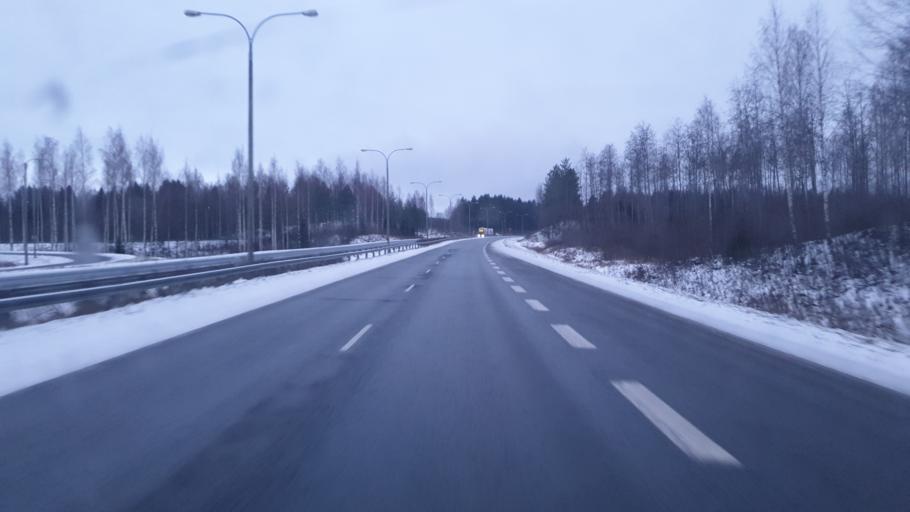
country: FI
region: Northern Savo
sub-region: Kuopio
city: Siilinjaervi
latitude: 63.0583
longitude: 27.6713
